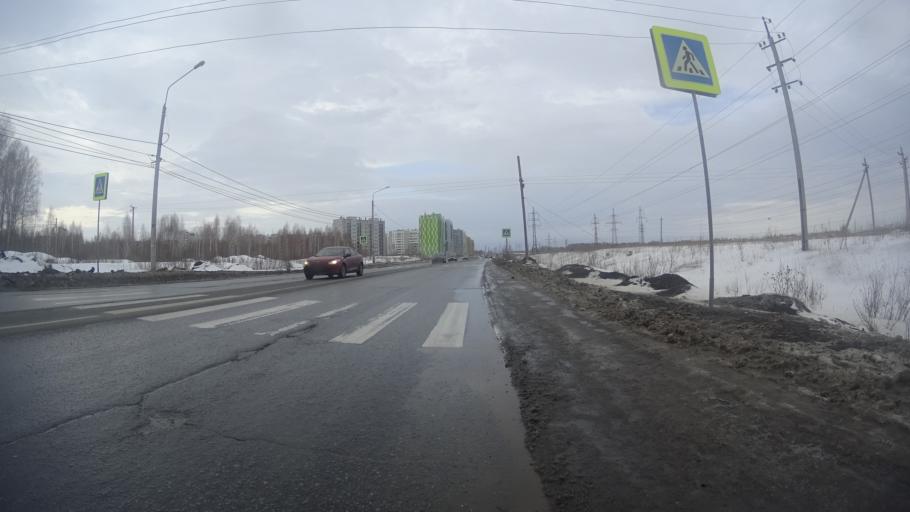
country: RU
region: Chelyabinsk
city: Roshchino
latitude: 55.2114
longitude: 61.3095
